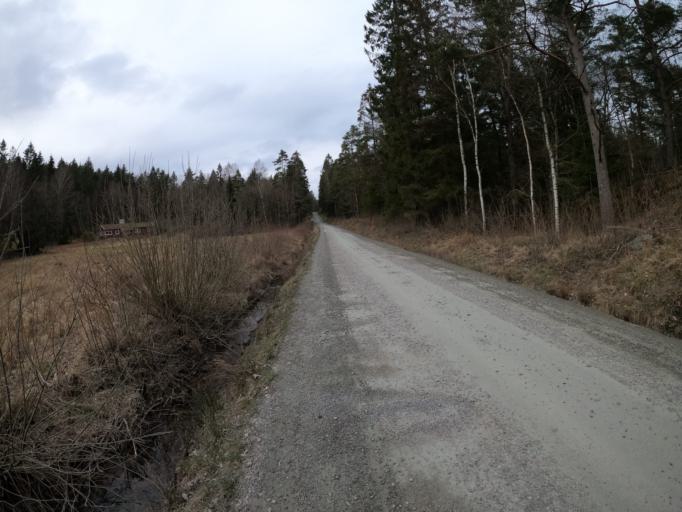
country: SE
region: Vaestra Goetaland
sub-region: Harryda Kommun
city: Molnlycke
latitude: 57.6355
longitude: 12.1010
